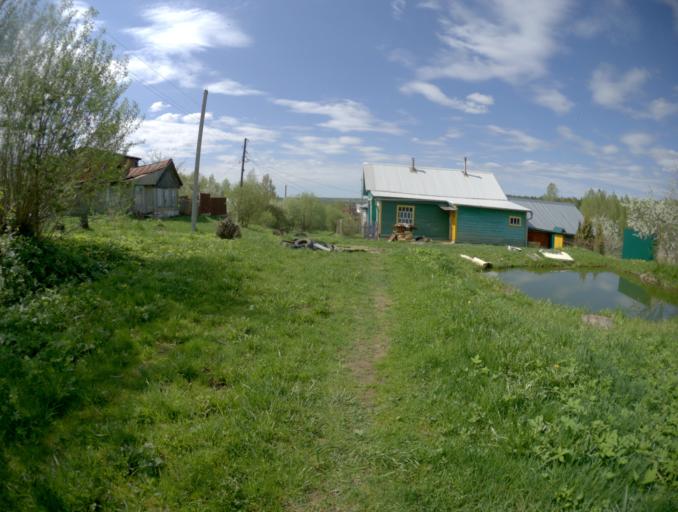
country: RU
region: Vladimir
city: Golovino
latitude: 56.0048
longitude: 40.4385
